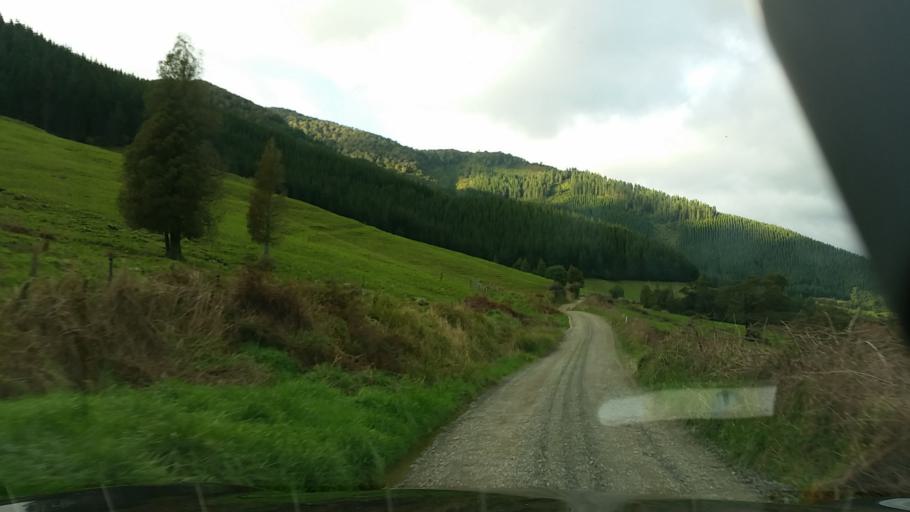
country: NZ
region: Nelson
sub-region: Nelson City
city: Nelson
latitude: -41.2088
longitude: 173.6336
